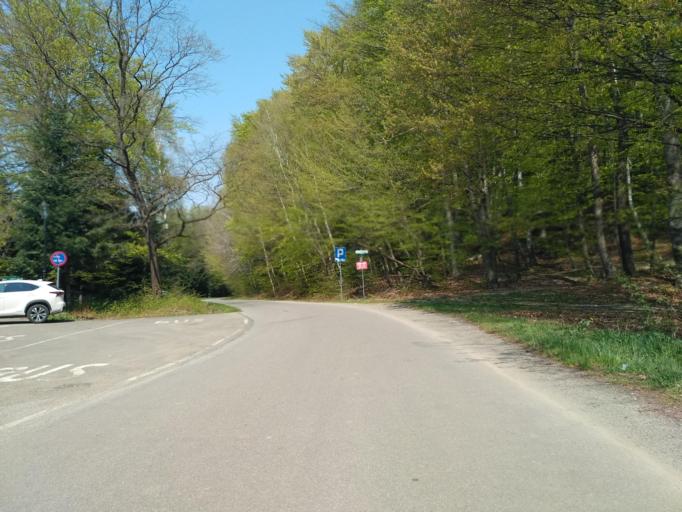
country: PL
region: Subcarpathian Voivodeship
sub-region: Powiat krosnienski
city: Chorkowka
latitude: 49.6161
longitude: 21.7117
